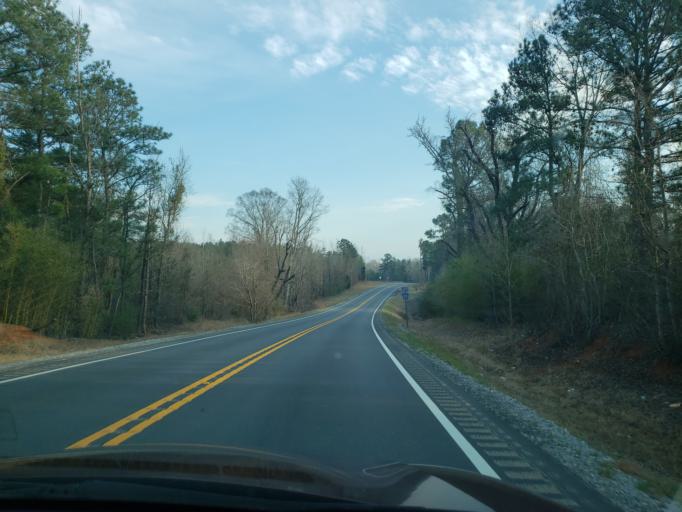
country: US
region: Alabama
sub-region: Hale County
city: Moundville
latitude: 32.8857
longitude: -87.6087
